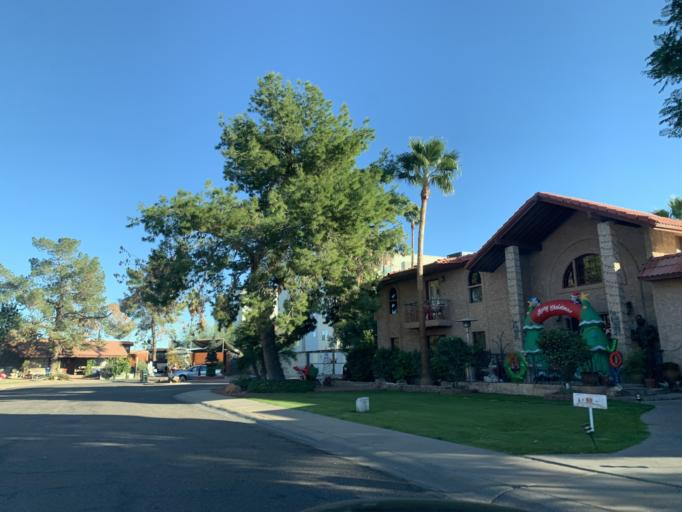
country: US
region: Arizona
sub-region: Maricopa County
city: Phoenix
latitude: 33.4493
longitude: -112.0605
